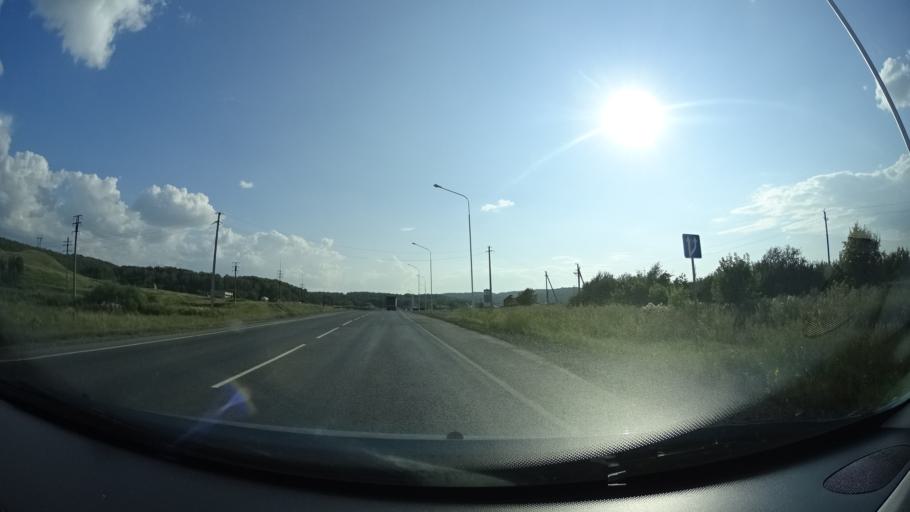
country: RU
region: Tatarstan
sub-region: Bavlinskiy Rayon
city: Bavly
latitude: 54.4624
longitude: 53.2879
